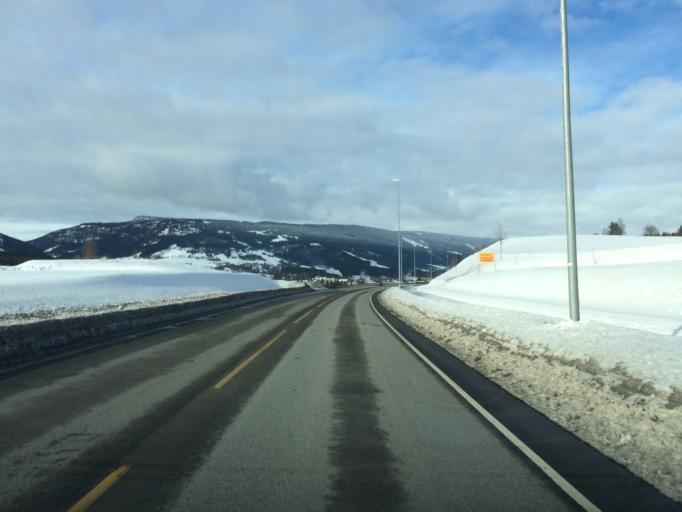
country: NO
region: Oppland
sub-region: Gausdal
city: Segalstad bru
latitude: 61.2211
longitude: 10.2431
